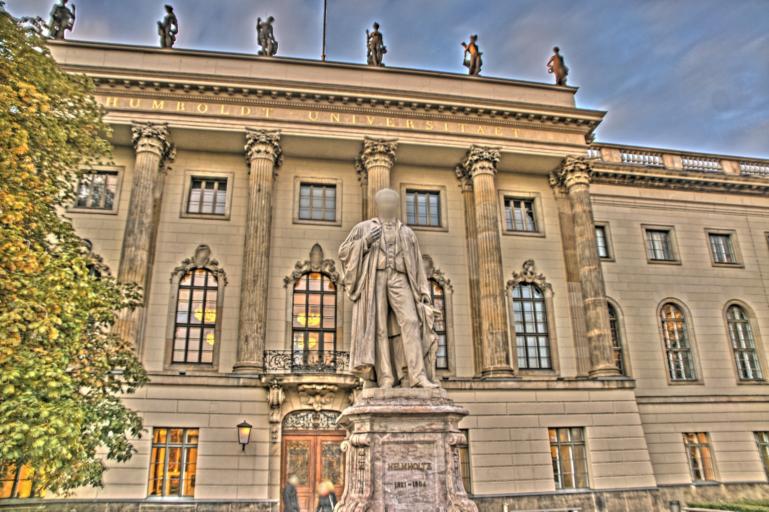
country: DE
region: Berlin
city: Mitte
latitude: 52.5177
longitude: 13.3938
